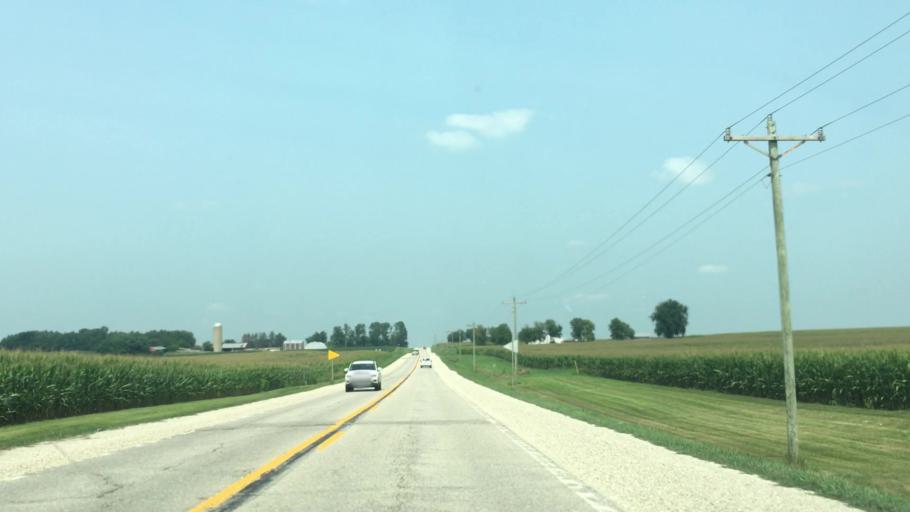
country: US
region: Iowa
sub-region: Benton County
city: Urbana
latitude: 42.3315
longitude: -91.8894
